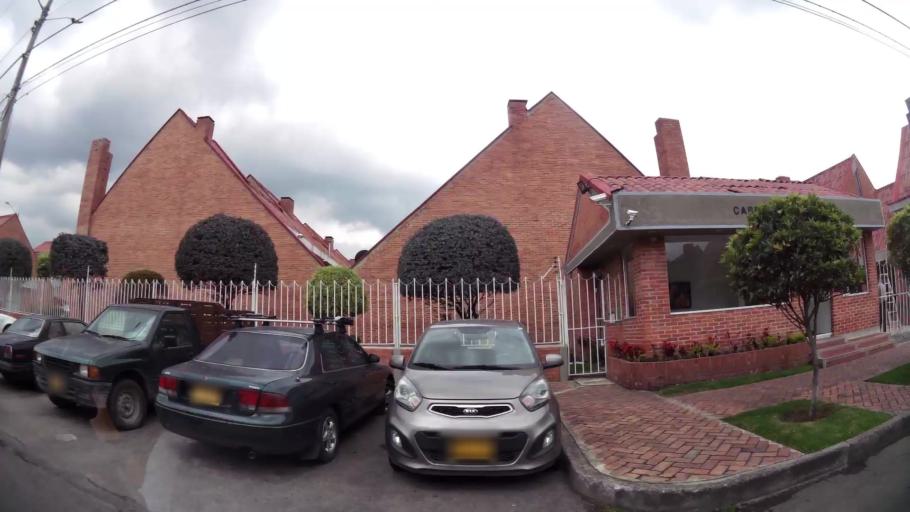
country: CO
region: Cundinamarca
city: Cota
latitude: 4.7654
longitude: -74.0416
